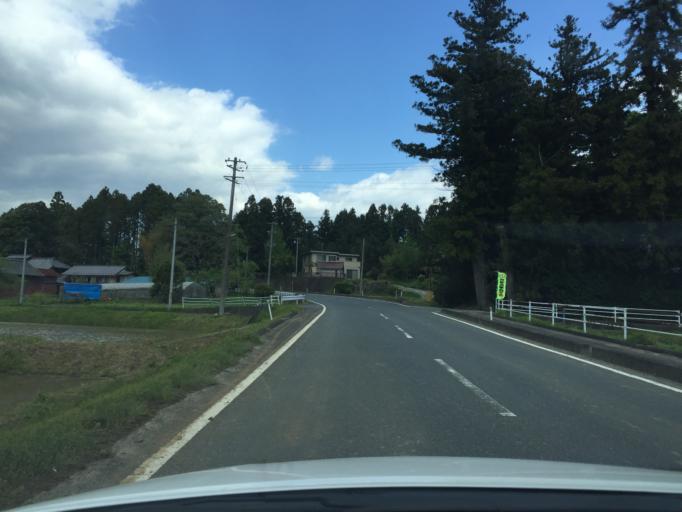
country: JP
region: Miyagi
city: Marumori
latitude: 37.7357
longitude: 140.9278
